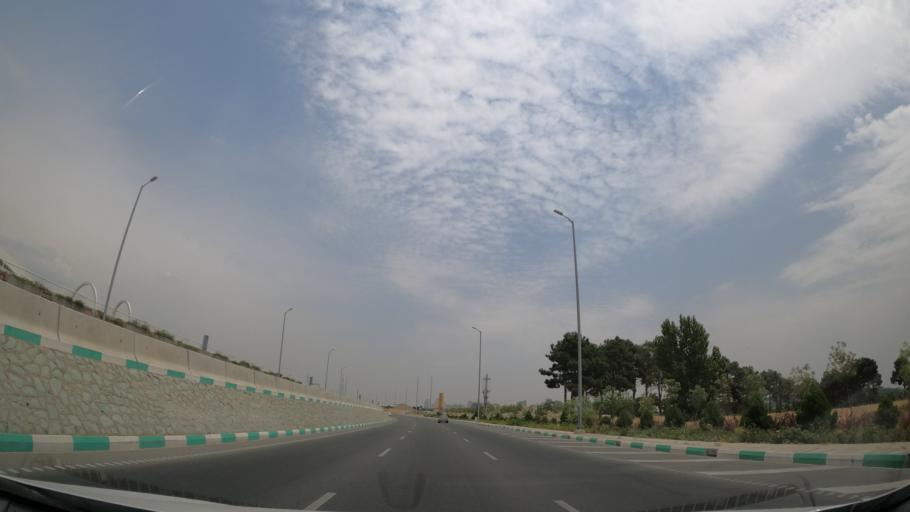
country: IR
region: Tehran
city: Shahr-e Qods
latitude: 35.7389
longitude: 51.2178
